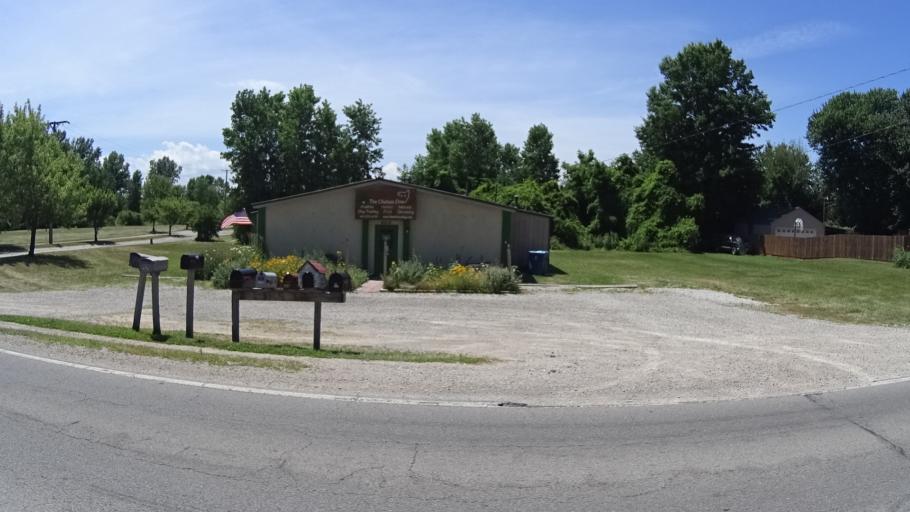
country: US
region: Ohio
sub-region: Erie County
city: Sandusky
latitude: 41.4045
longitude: -82.6802
